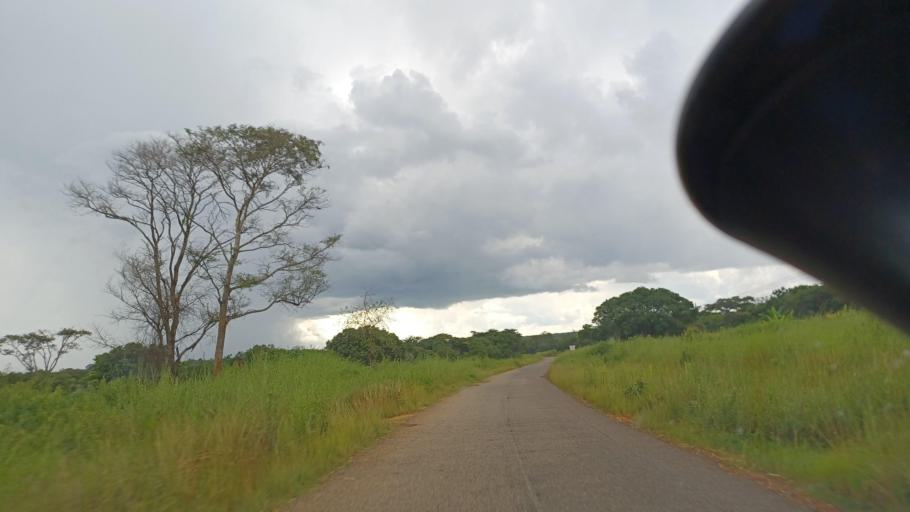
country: ZM
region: North-Western
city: Kasempa
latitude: -13.0101
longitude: 26.0065
